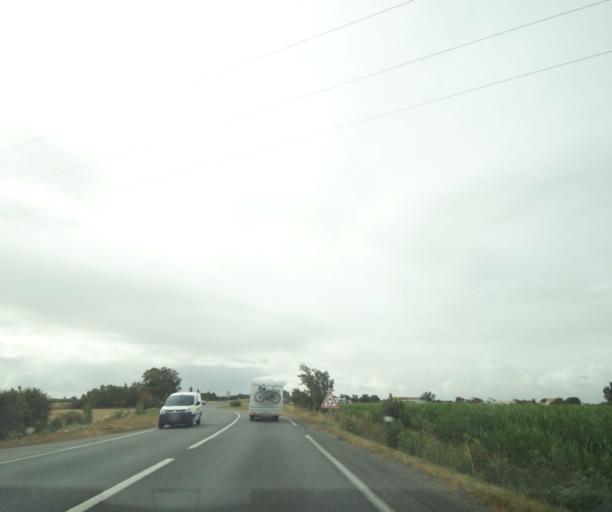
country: FR
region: Pays de la Loire
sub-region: Departement de la Vendee
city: Champagne-les-Marais
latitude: 46.4282
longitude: -1.0929
